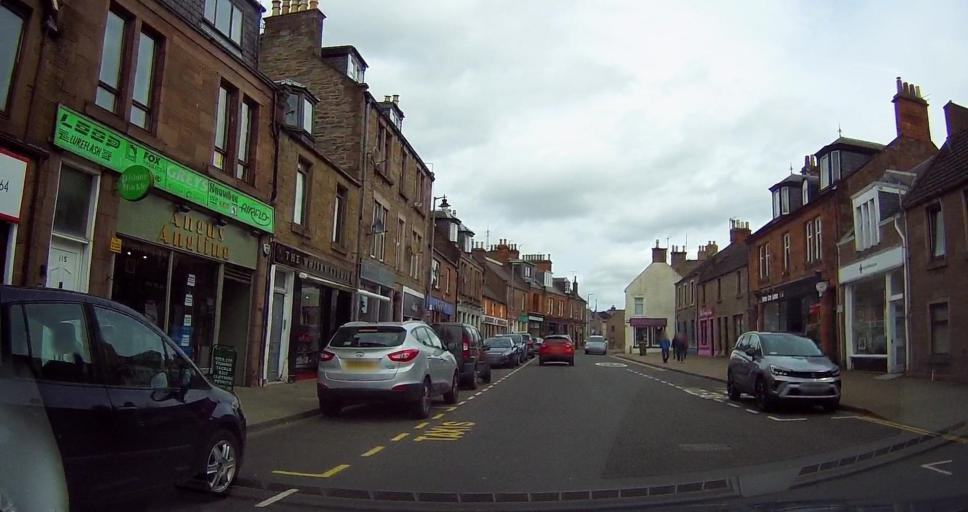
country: GB
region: Scotland
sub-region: Angus
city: Forfar
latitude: 56.6450
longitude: -2.8839
